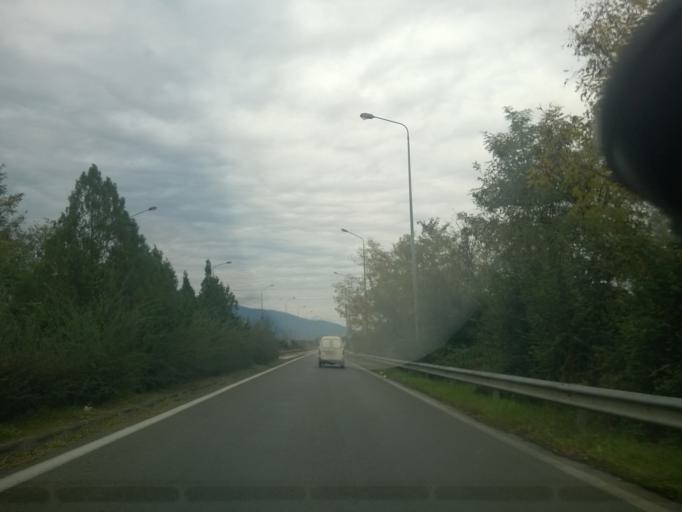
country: GR
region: Central Macedonia
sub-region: Nomos Pellis
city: Mavrovouni
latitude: 40.7883
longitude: 22.1632
